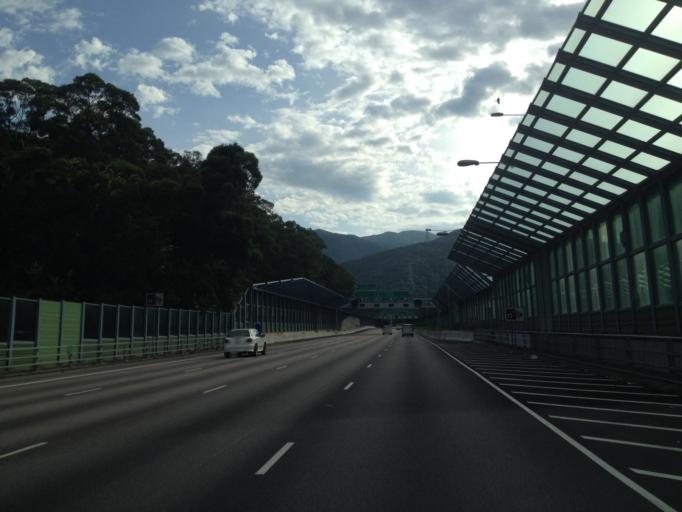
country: HK
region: Tai Po
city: Tai Po
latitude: 22.4419
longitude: 114.1706
